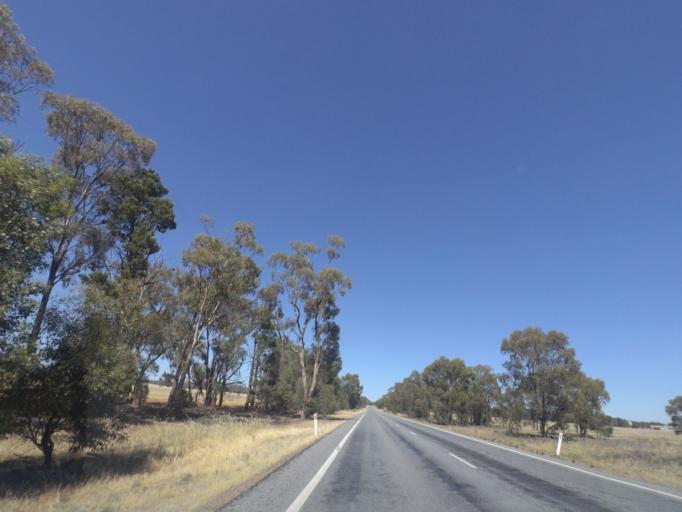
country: AU
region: New South Wales
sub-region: Narrandera
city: Narrandera
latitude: -34.4162
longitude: 146.8583
